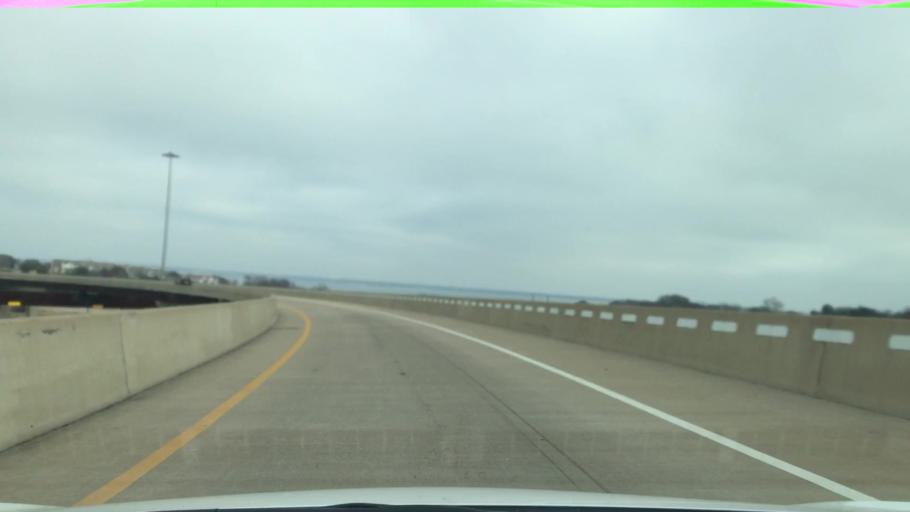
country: US
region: Texas
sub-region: Dallas County
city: Rowlett
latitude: 32.8589
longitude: -96.5531
